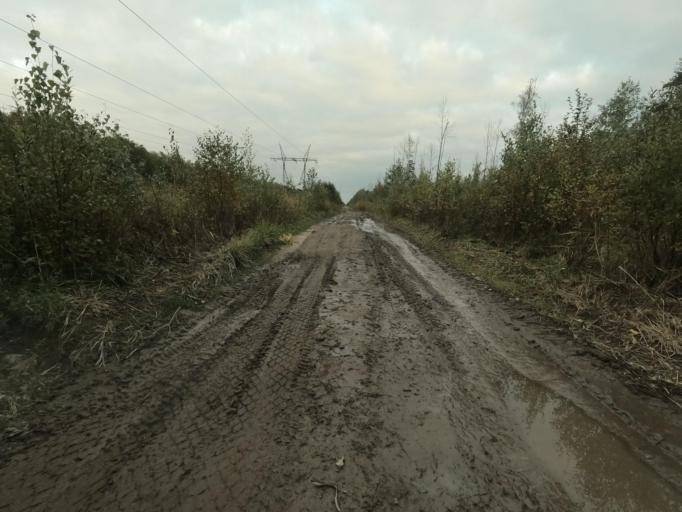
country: RU
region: St.-Petersburg
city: Sapernyy
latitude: 59.7558
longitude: 30.6831
